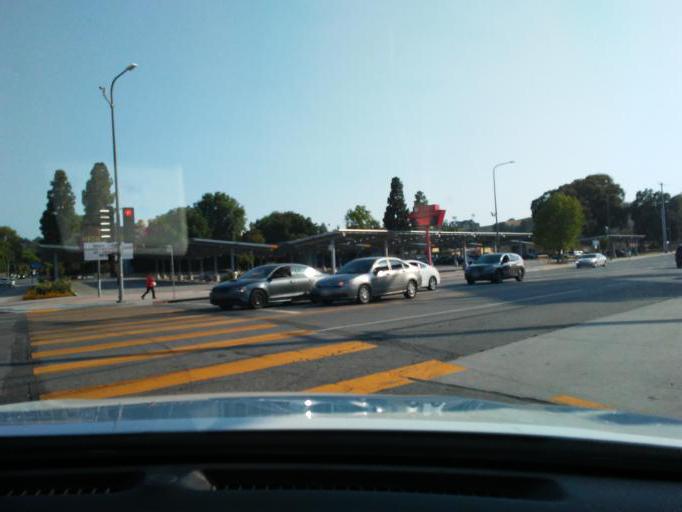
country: US
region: California
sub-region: Los Angeles County
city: Woodland Hills
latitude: 34.1711
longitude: -118.5710
